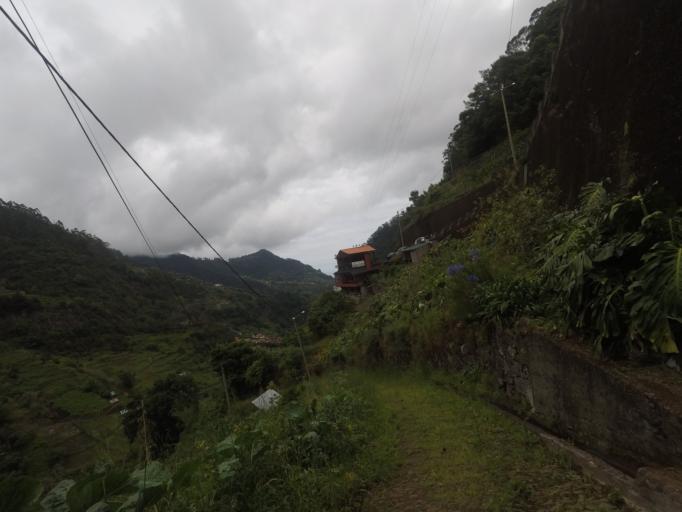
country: PT
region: Madeira
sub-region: Santana
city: Santana
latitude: 32.7600
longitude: -16.8778
